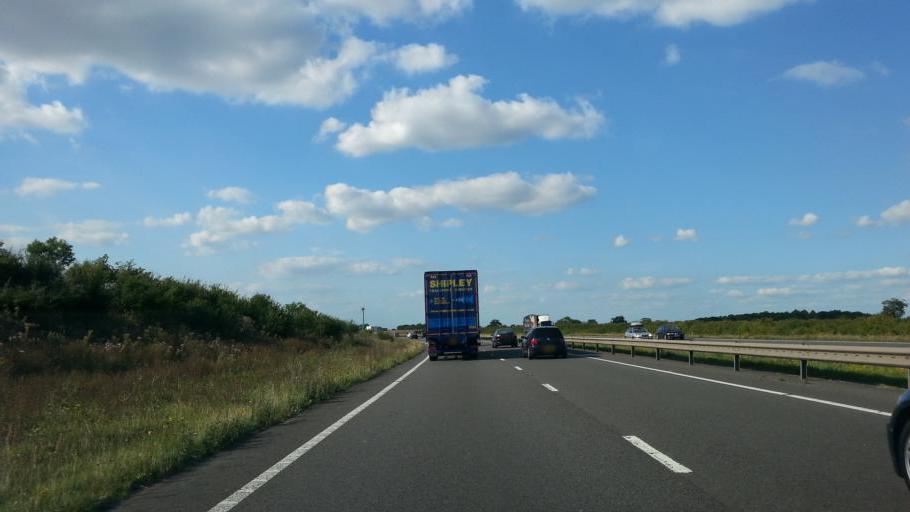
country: GB
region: England
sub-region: Lincolnshire
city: Great Gonerby
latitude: 52.9505
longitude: -0.6825
